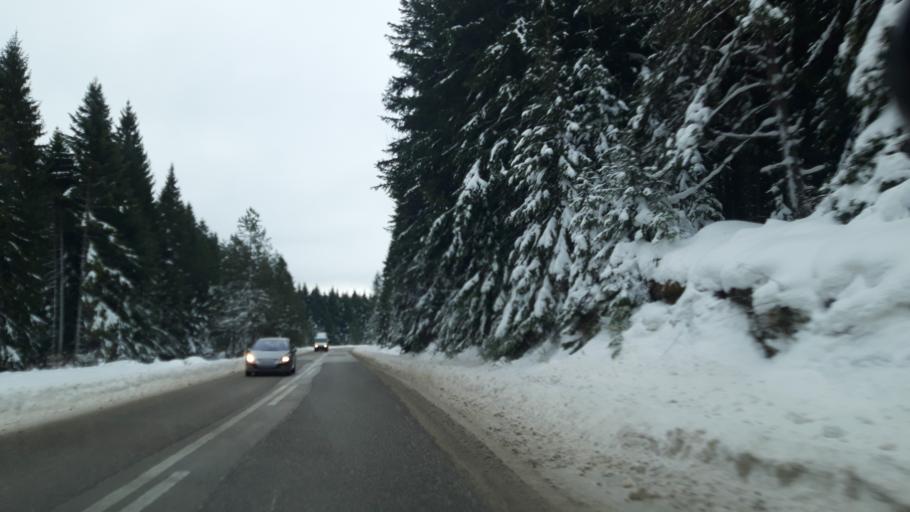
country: BA
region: Republika Srpska
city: Han Pijesak
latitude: 44.0463
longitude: 18.9291
